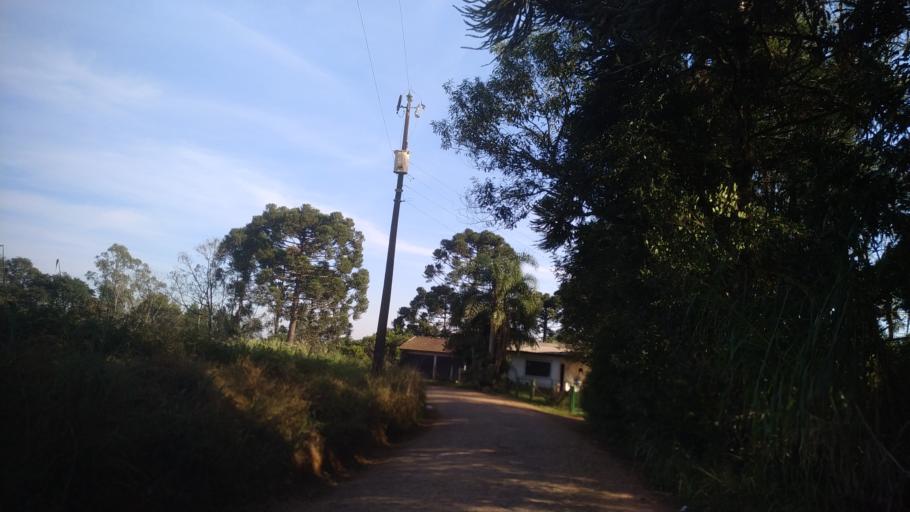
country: BR
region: Santa Catarina
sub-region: Chapeco
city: Chapeco
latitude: -27.1250
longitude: -52.6314
